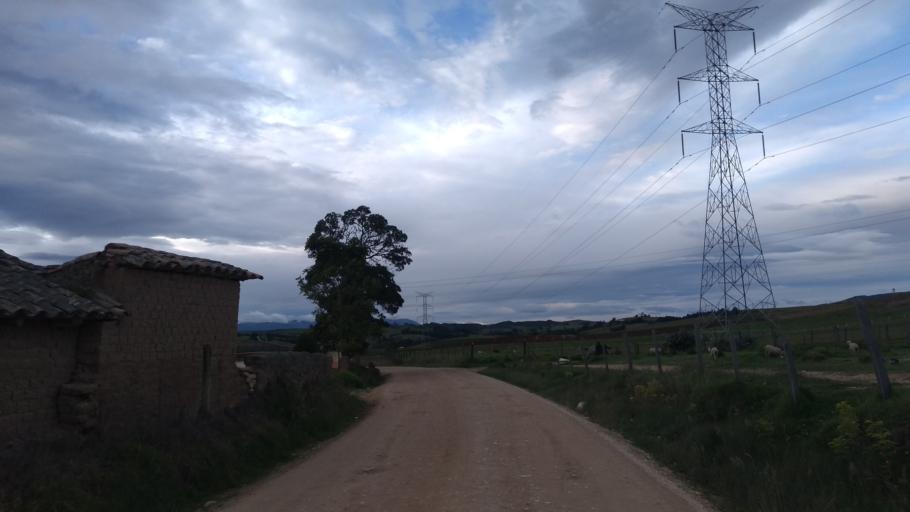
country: CO
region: Boyaca
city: Toca
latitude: 5.6048
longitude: -73.1774
